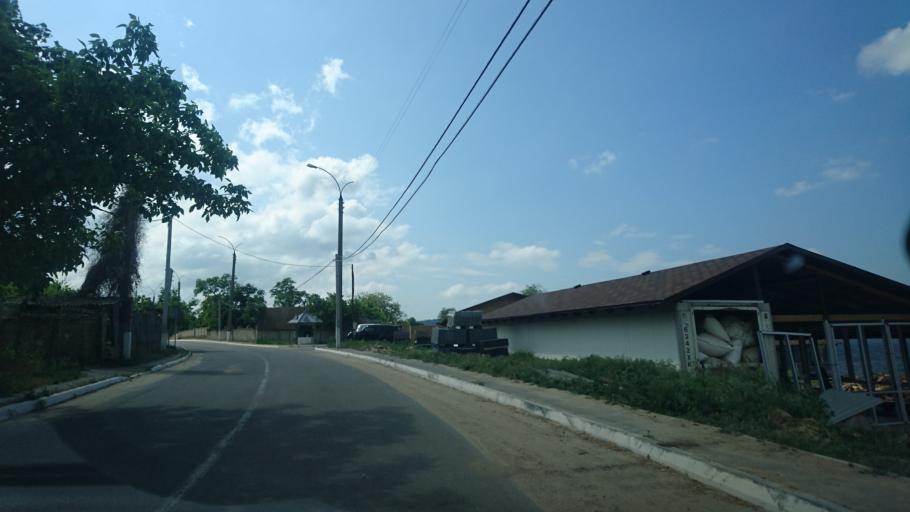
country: MD
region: Telenesti
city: Cocieri
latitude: 47.3503
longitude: 29.1079
